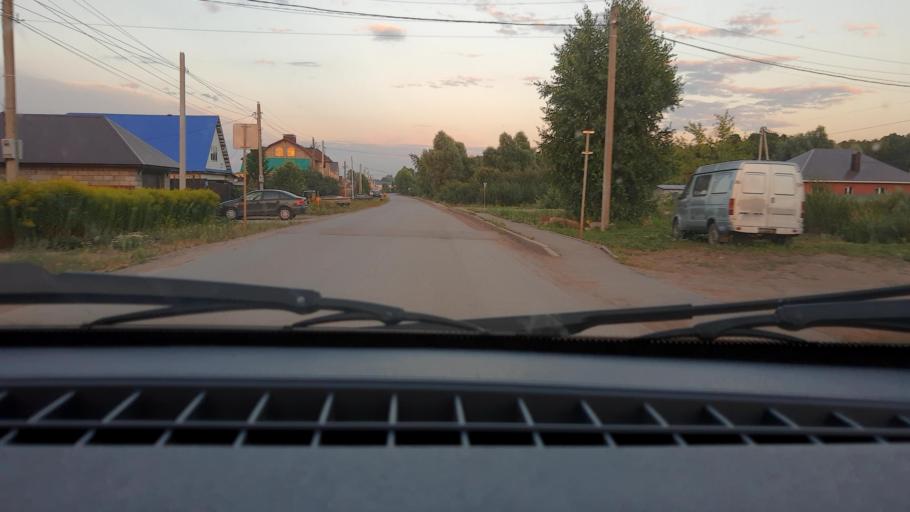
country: RU
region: Bashkortostan
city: Mikhaylovka
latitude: 54.7853
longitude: 55.8144
